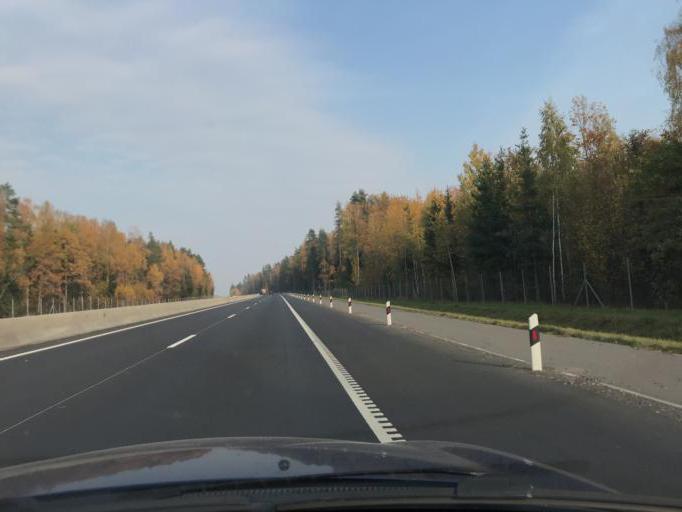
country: BY
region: Grodnenskaya
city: Shchuchin
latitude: 53.6675
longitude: 24.8242
